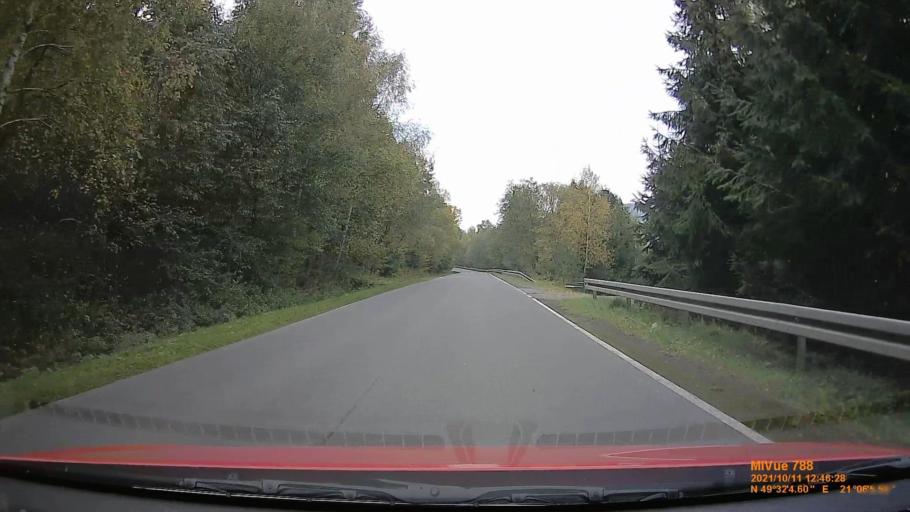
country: PL
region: Lesser Poland Voivodeship
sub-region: Powiat gorlicki
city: Uscie Gorlickie
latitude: 49.5347
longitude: 21.1014
